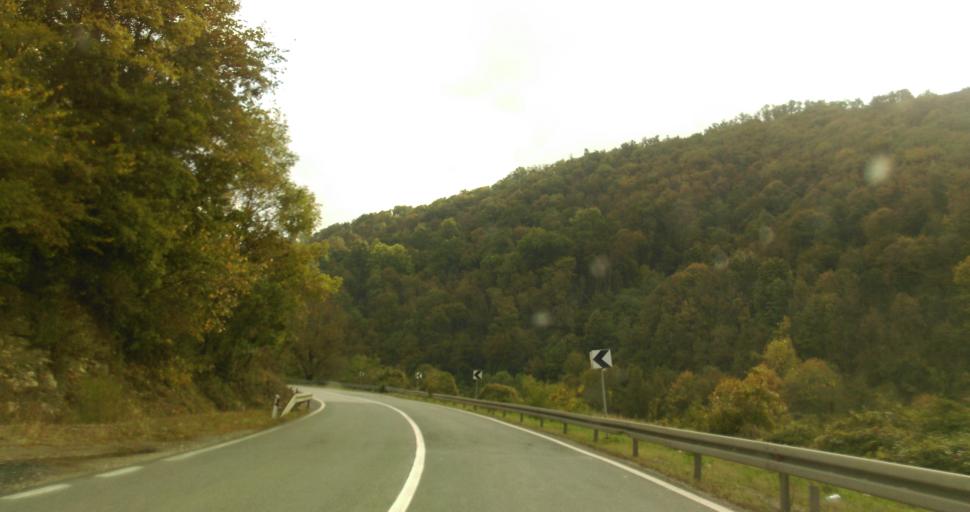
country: RS
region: Central Serbia
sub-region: Kolubarski Okrug
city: Ljig
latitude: 44.1900
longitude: 20.3149
